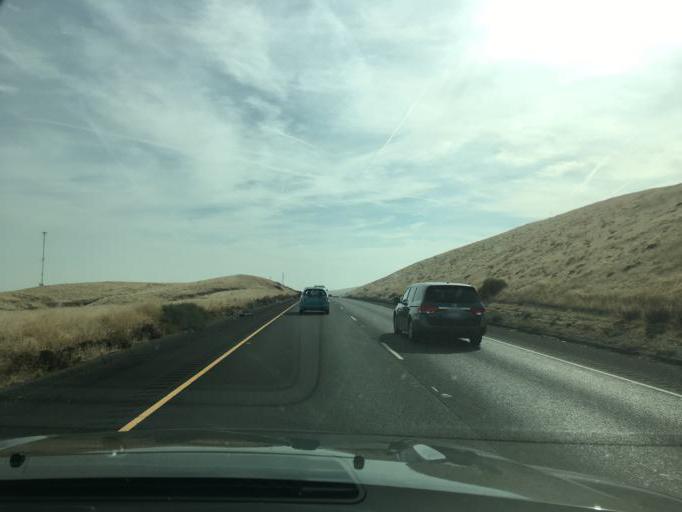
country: US
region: California
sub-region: Kings County
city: Kettleman City
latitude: 35.9985
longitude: -119.9778
